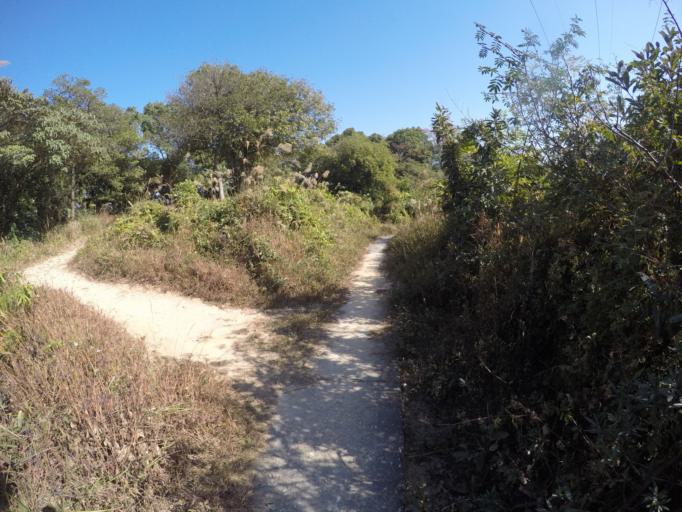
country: CN
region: Guangdong
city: Dongqu
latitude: 22.5332
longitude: 113.4033
